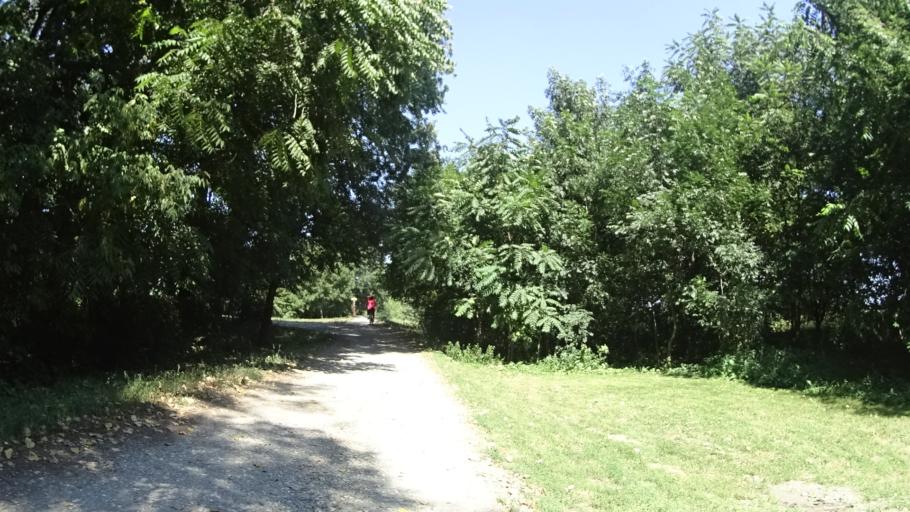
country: CZ
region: South Moravian
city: Straznice
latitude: 48.9085
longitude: 17.3218
